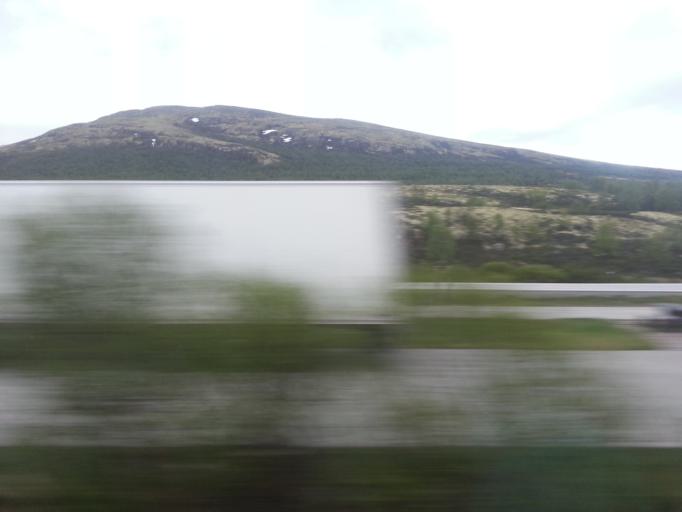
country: NO
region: Sor-Trondelag
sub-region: Oppdal
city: Oppdal
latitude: 62.2557
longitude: 9.5465
